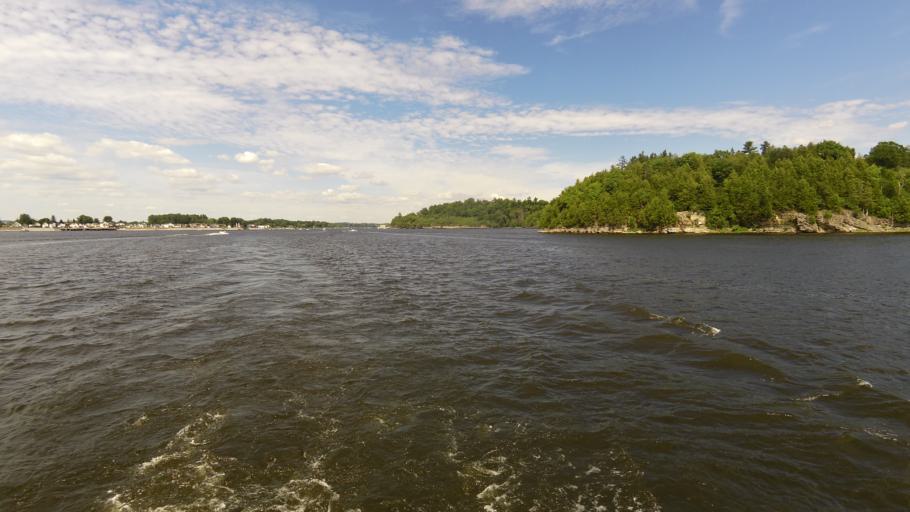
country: CA
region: Quebec
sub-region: Outaouais
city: Gatineau
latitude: 45.4481
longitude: -75.6956
